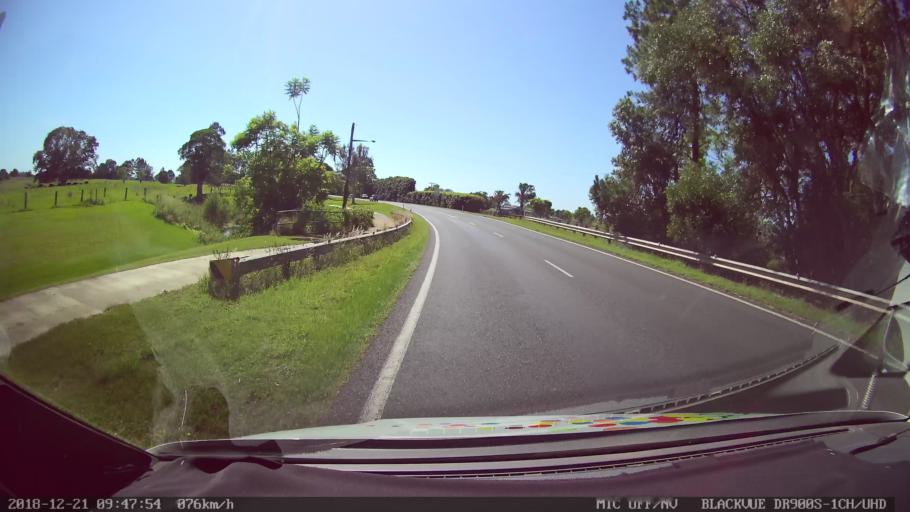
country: AU
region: New South Wales
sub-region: Clarence Valley
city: Grafton
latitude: -29.6505
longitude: 152.9277
